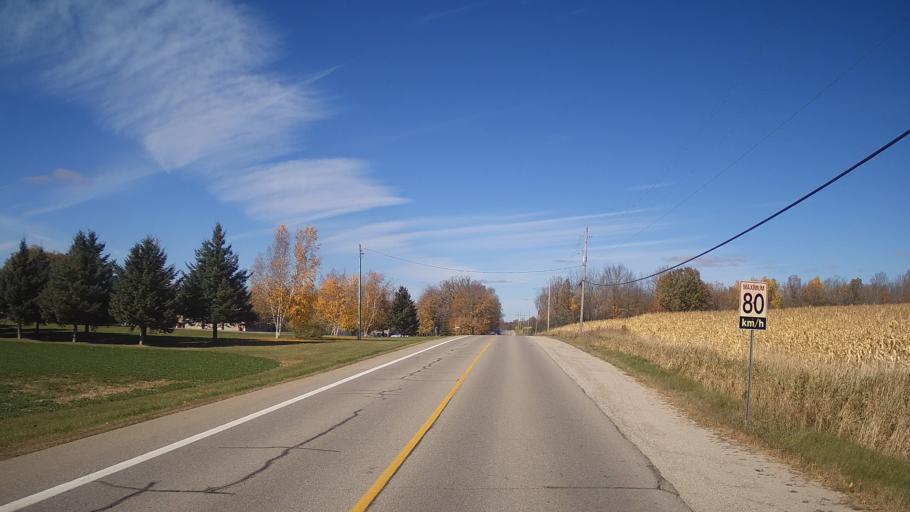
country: CA
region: Ontario
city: Perth
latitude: 44.8647
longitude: -76.2858
